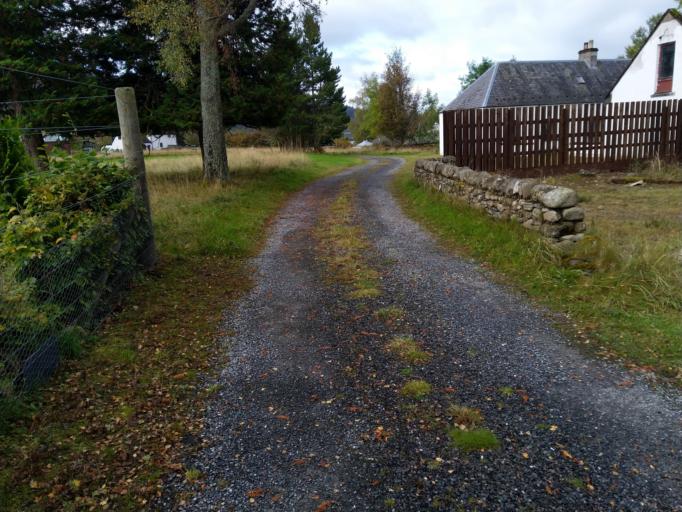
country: GB
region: Scotland
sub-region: Perth and Kinross
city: Aberfeldy
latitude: 56.6990
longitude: -4.1862
